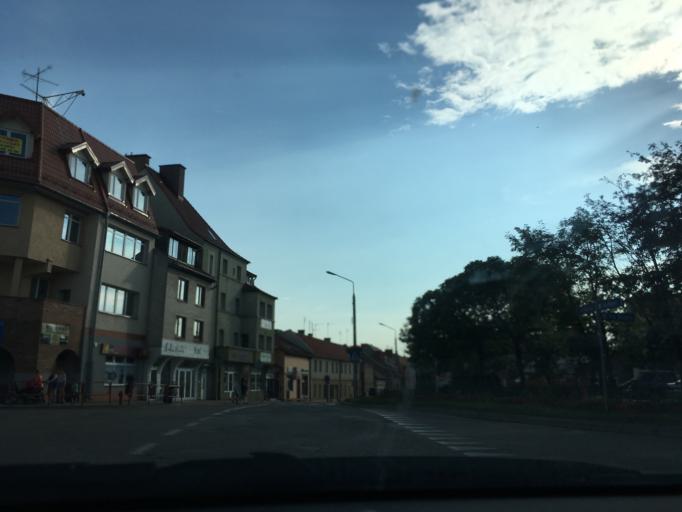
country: PL
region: Warmian-Masurian Voivodeship
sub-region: Powiat olecki
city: Olecko
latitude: 54.0363
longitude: 22.5046
